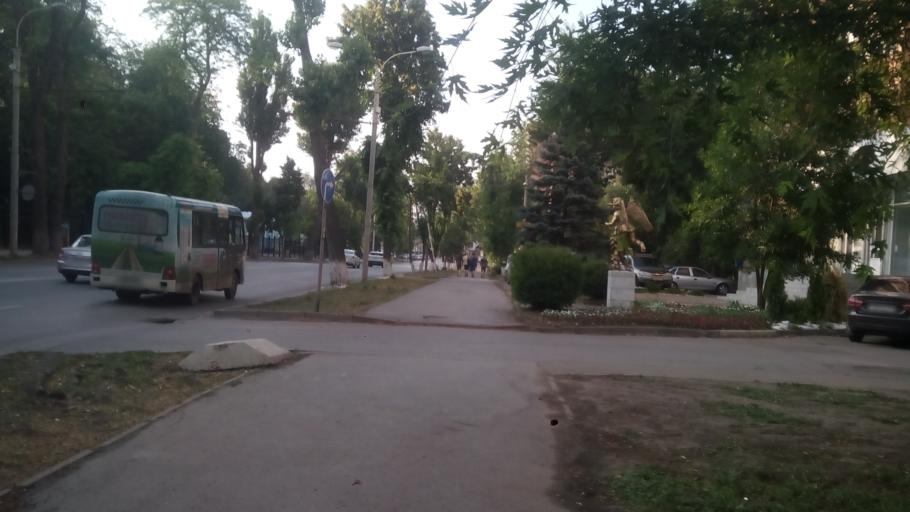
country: RU
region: Rostov
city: Imeni Chkalova
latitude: 47.2465
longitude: 39.7653
